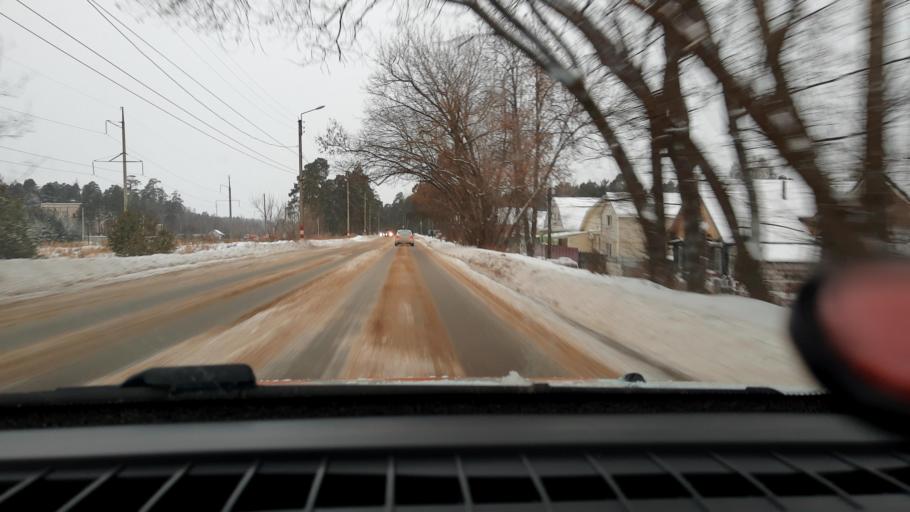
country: RU
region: Nizjnij Novgorod
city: Bor
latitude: 56.3276
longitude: 44.1290
